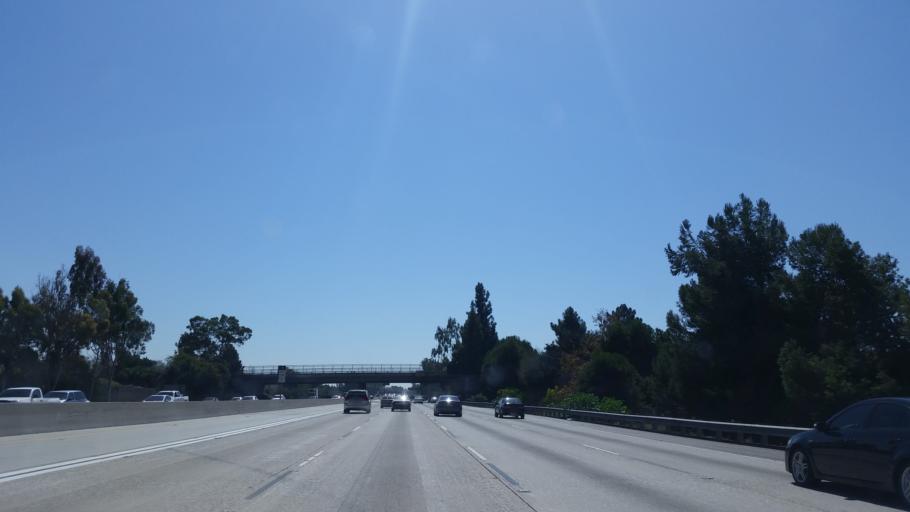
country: US
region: California
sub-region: Los Angeles County
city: Hawaiian Gardens
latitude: 33.8198
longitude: -118.0815
